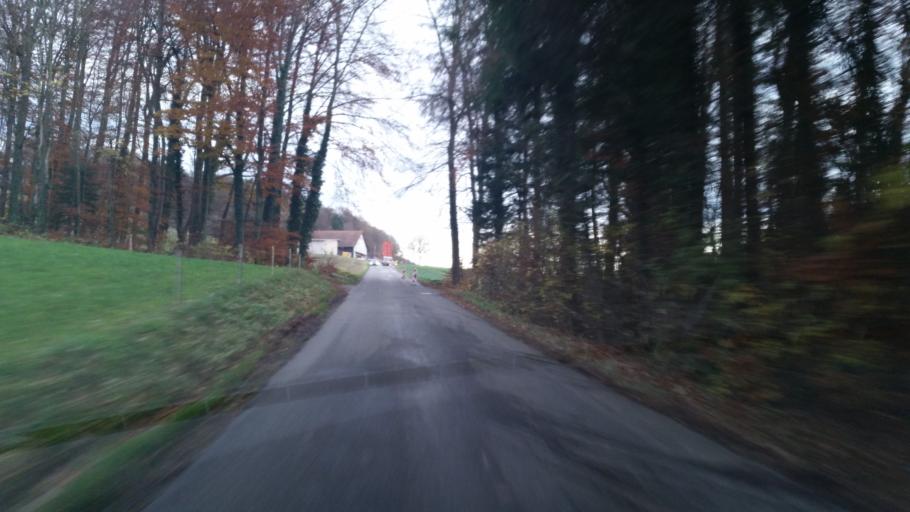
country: CH
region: Aargau
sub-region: Bezirk Baden
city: Kunten
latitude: 47.3844
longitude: 8.3398
